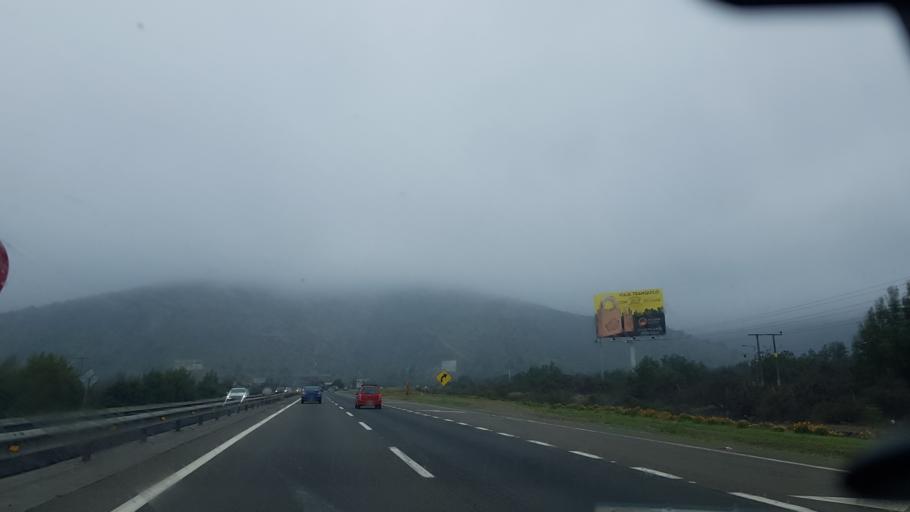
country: CL
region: Santiago Metropolitan
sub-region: Provincia de Talagante
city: Penaflor
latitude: -33.4574
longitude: -70.9227
